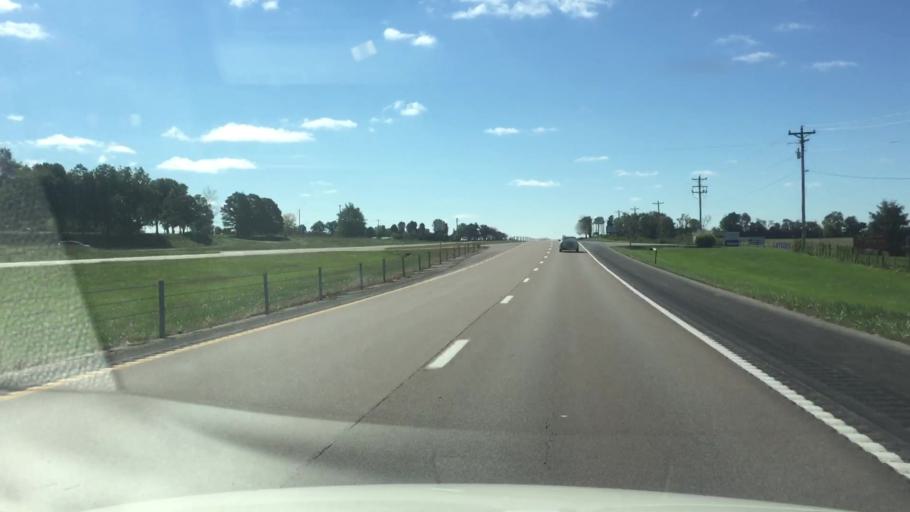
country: US
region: Missouri
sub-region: Boone County
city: Ashland
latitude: 38.7901
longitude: -92.2523
